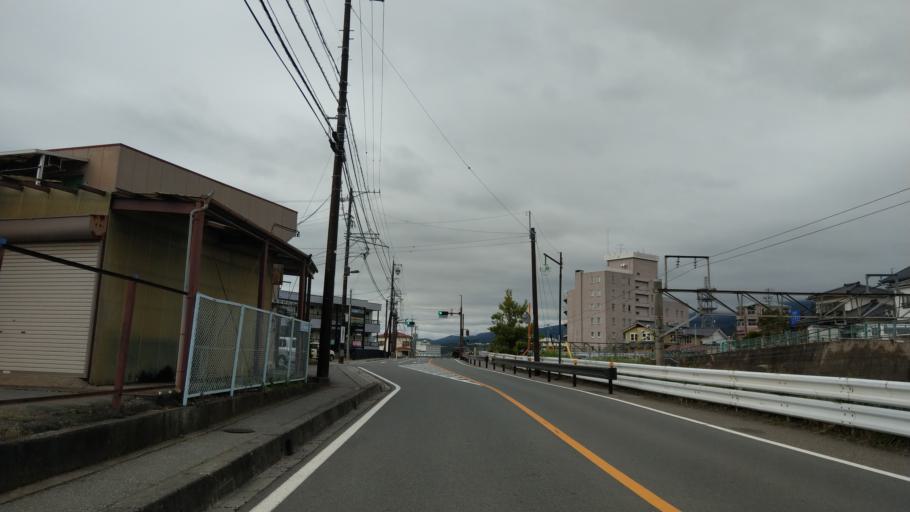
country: JP
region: Nagano
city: Komoro
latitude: 36.3221
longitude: 138.4266
